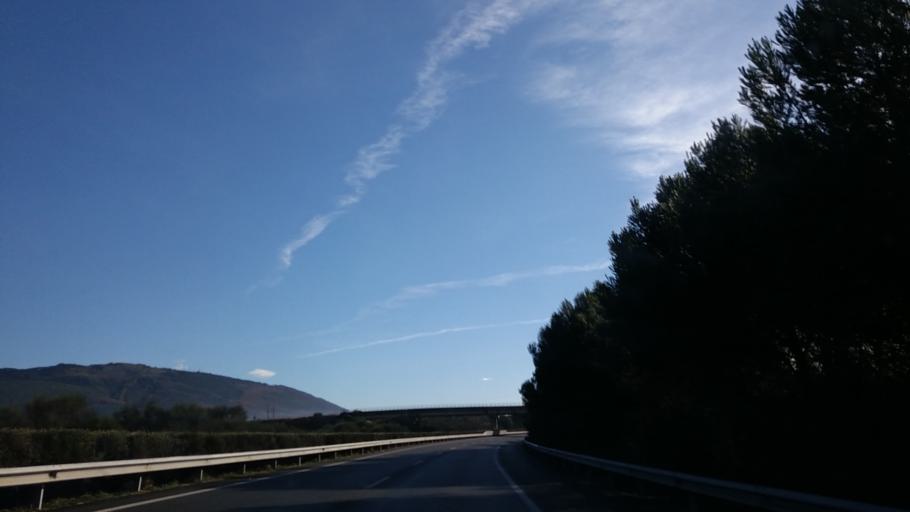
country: ES
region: Navarre
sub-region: Provincia de Navarra
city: Berriobeiti
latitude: 42.8536
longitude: -1.7145
